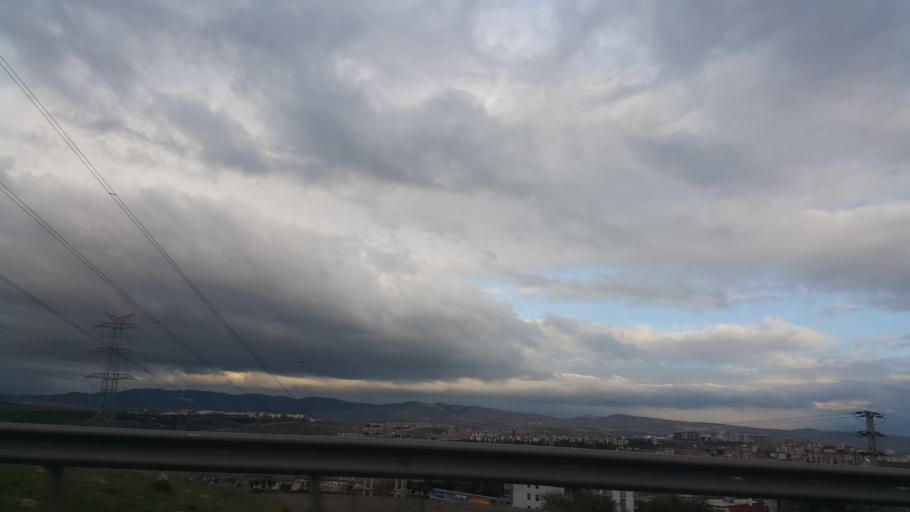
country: TR
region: Ankara
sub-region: Goelbasi
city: Golbasi
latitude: 39.8077
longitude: 32.8010
